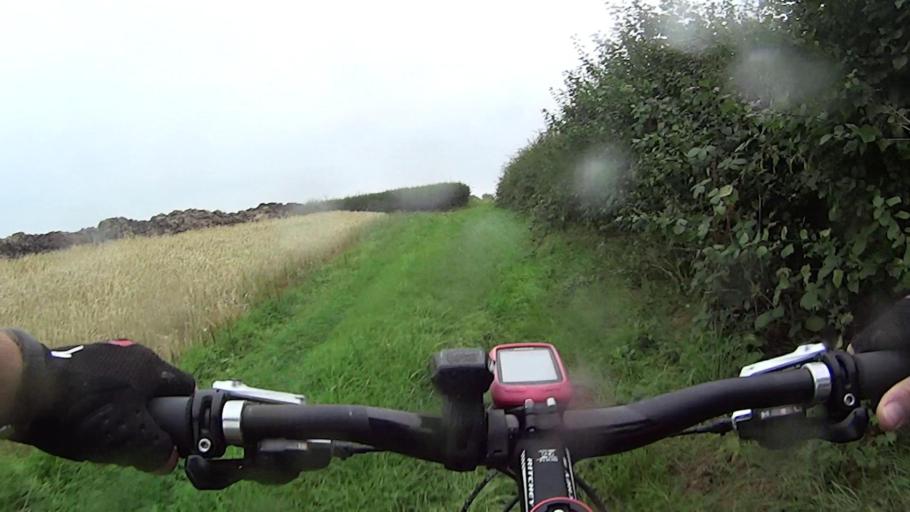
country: GB
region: England
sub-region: Worcestershire
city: Tenbury Wells
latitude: 52.2926
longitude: -2.5733
